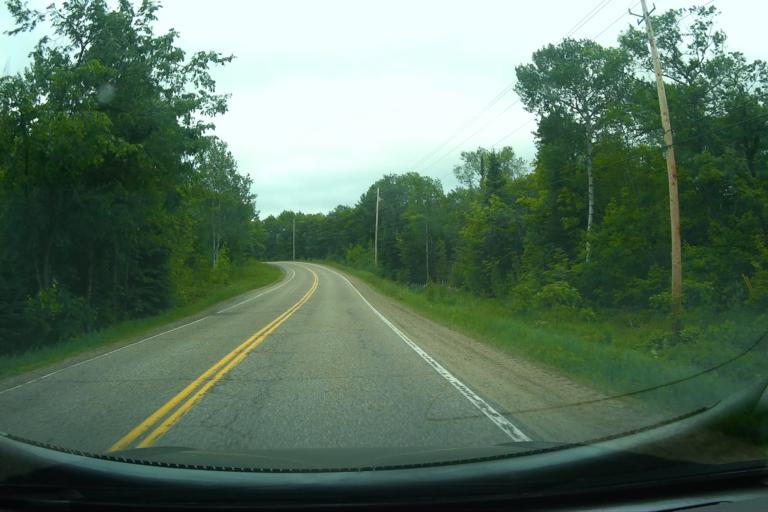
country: CA
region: Ontario
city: Pembroke
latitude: 45.4777
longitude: -77.2163
